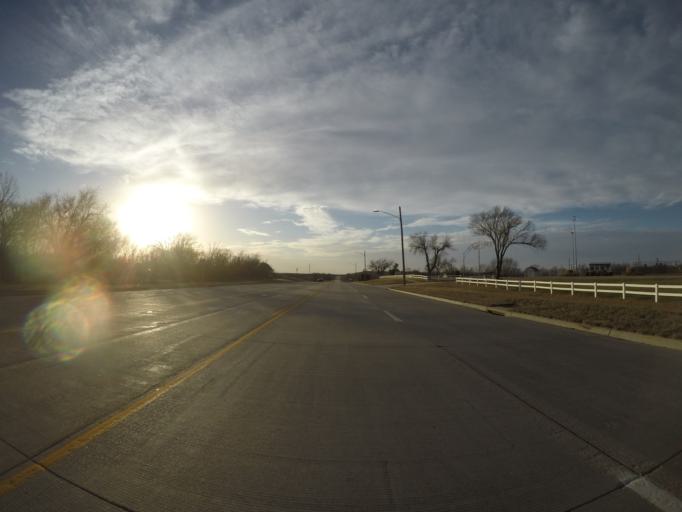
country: US
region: Kansas
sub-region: Chase County
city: Cottonwood Falls
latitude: 38.4001
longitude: -96.5359
